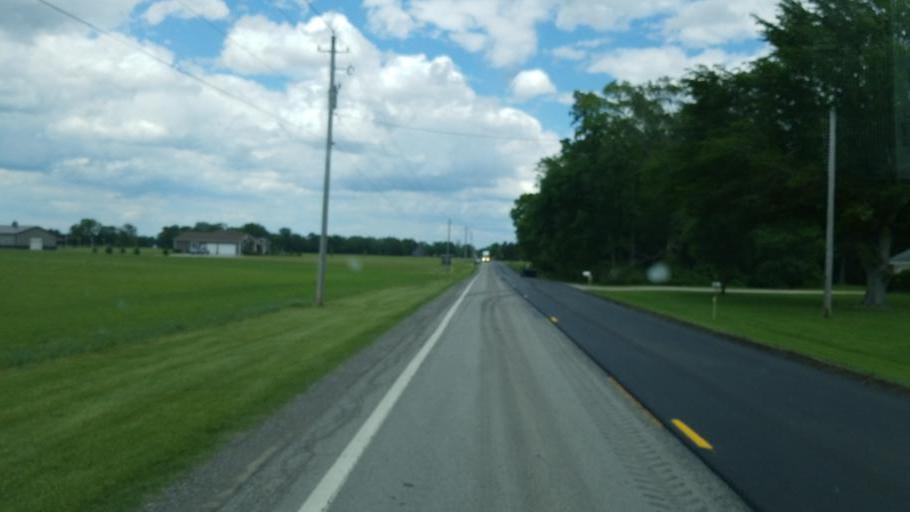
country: US
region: Ohio
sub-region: Erie County
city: Milan
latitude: 41.2995
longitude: -82.6263
